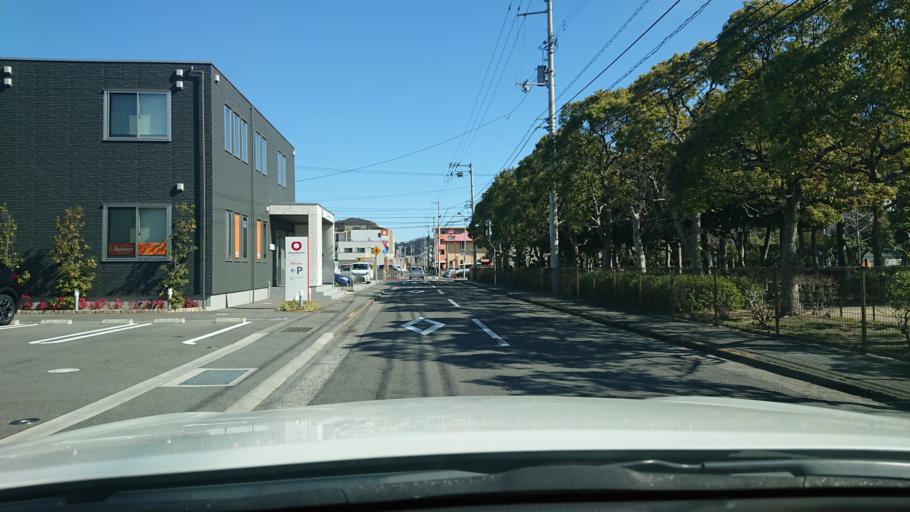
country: JP
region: Tokushima
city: Tokushima-shi
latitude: 34.0513
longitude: 134.5550
